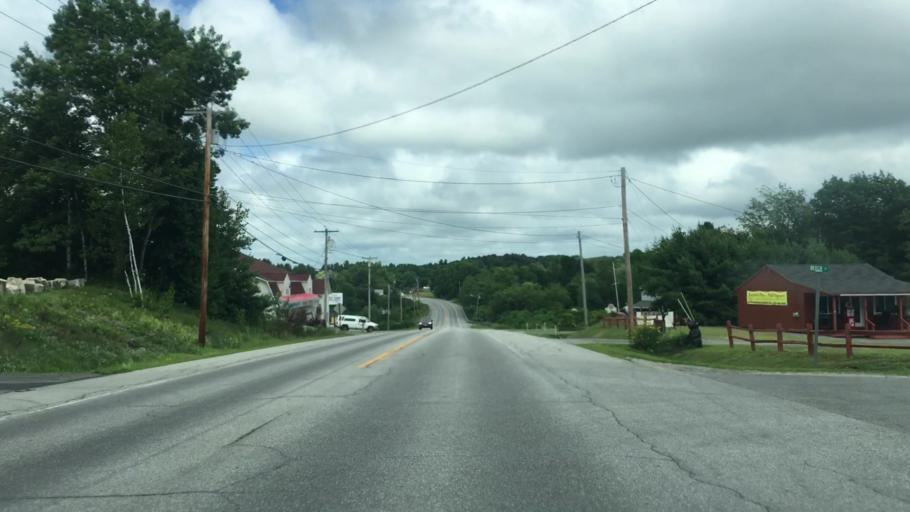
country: US
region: Maine
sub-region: Kennebec County
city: Hallowell
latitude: 44.2899
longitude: -69.7730
